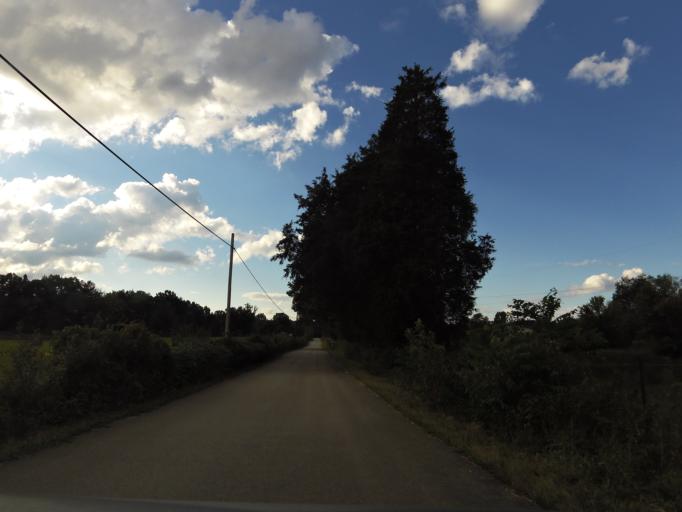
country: US
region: Tennessee
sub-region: Union County
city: Condon
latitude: 36.1257
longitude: -83.7764
